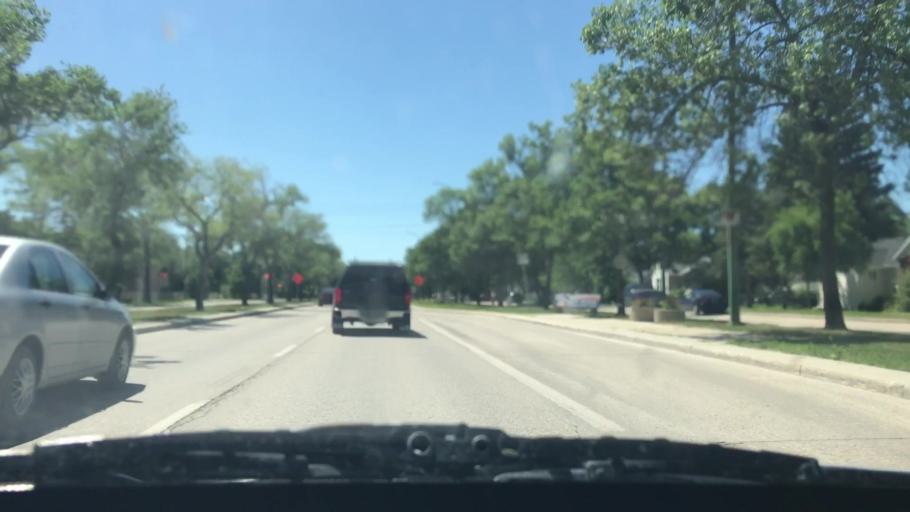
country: CA
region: Manitoba
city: Winnipeg
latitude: 49.8543
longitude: -97.1070
